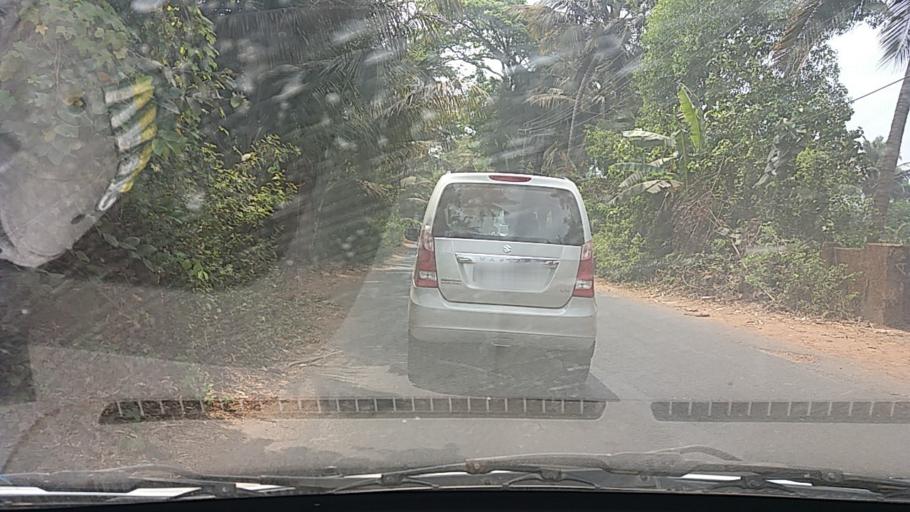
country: IN
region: Goa
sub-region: North Goa
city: Saligao
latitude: 15.5450
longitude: 73.7891
